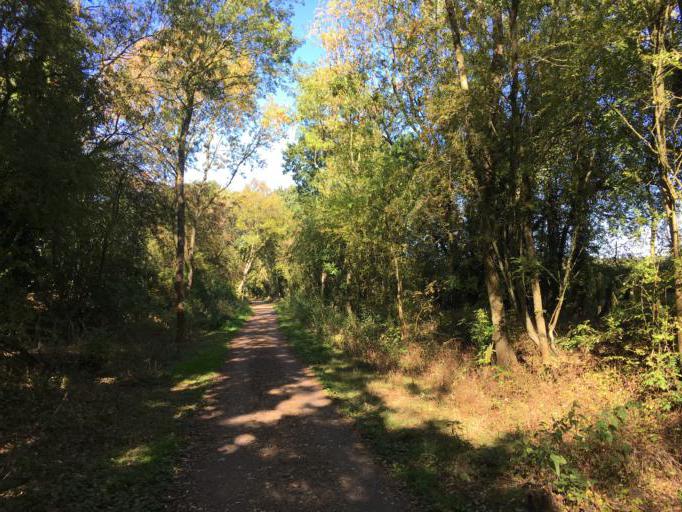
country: GB
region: England
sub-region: Warwickshire
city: Kenilworth
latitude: 52.3772
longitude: -1.6015
